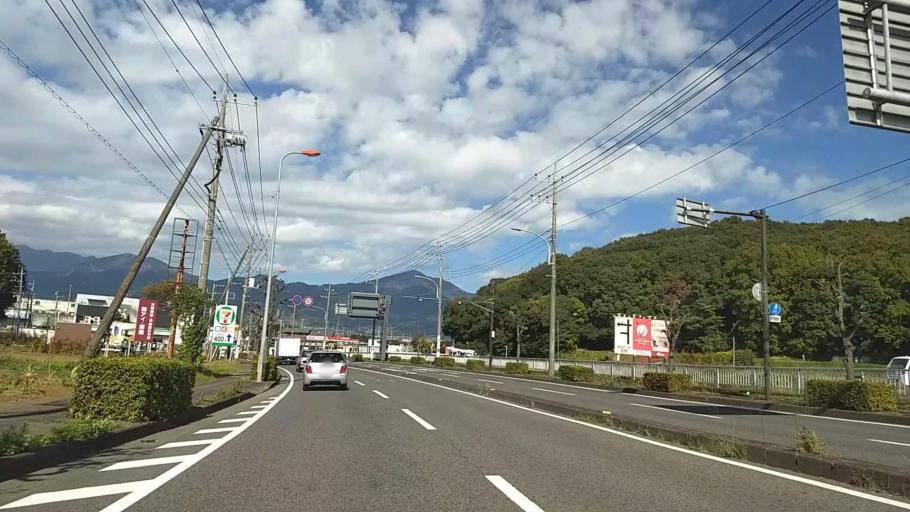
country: JP
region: Kanagawa
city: Hadano
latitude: 35.3551
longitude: 139.2364
